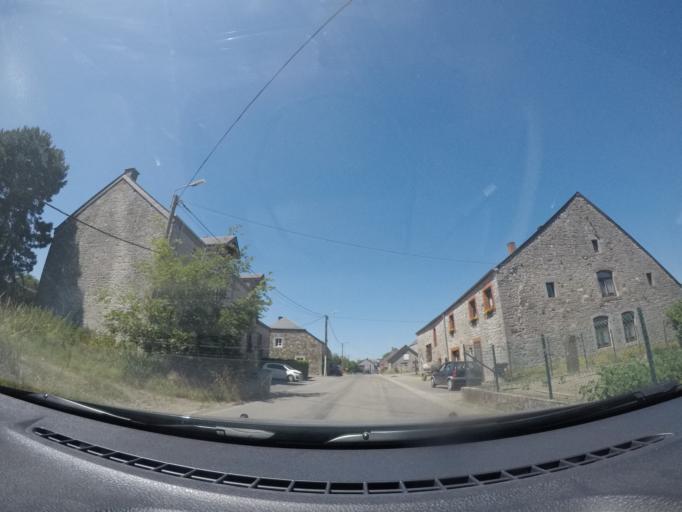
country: BE
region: Wallonia
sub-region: Province du Luxembourg
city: Wellin
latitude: 50.0754
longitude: 5.1347
